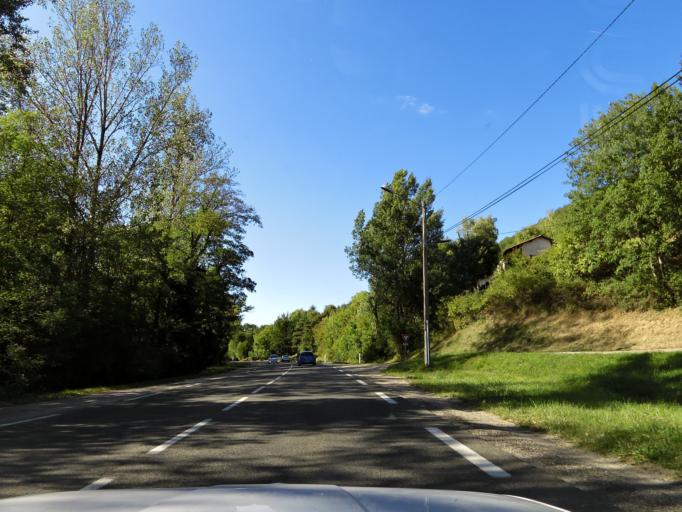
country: FR
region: Rhone-Alpes
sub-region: Departement de l'Ain
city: Vaux-en-Bugey
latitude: 45.9432
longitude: 5.3746
